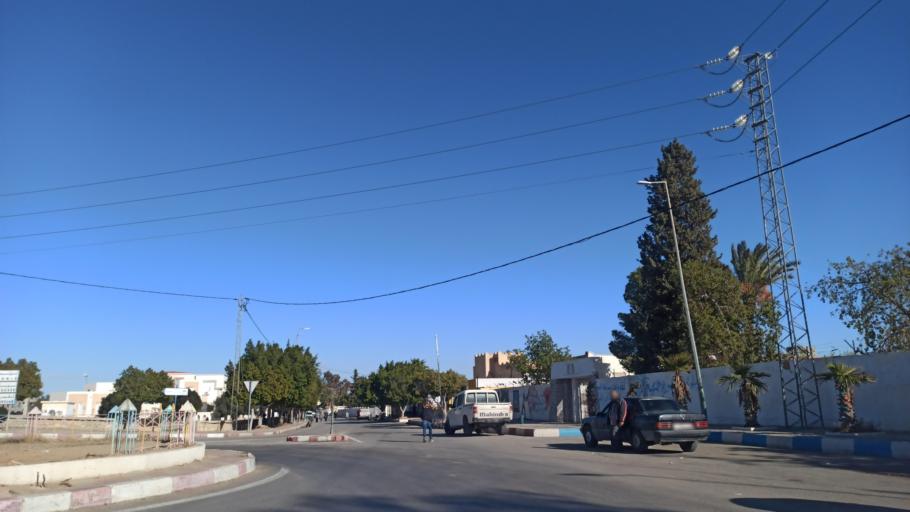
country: TN
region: Sidi Bu Zayd
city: Jilma
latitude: 35.2696
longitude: 9.4186
